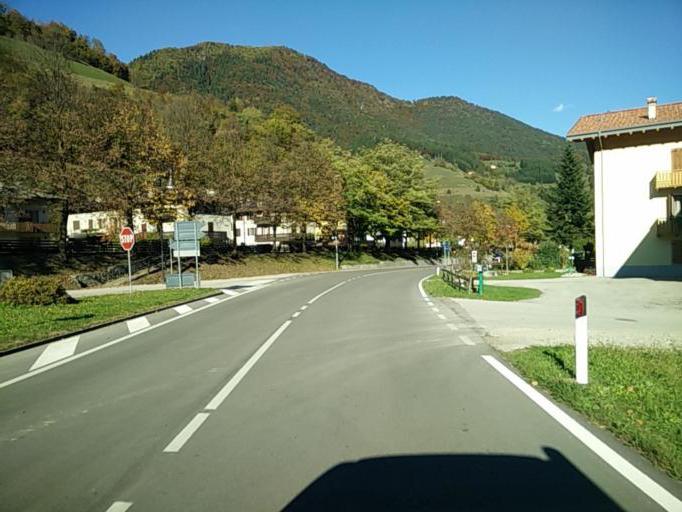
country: IT
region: Trentino-Alto Adige
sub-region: Provincia di Trento
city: Pieve di Ledro
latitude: 45.8913
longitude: 10.6755
